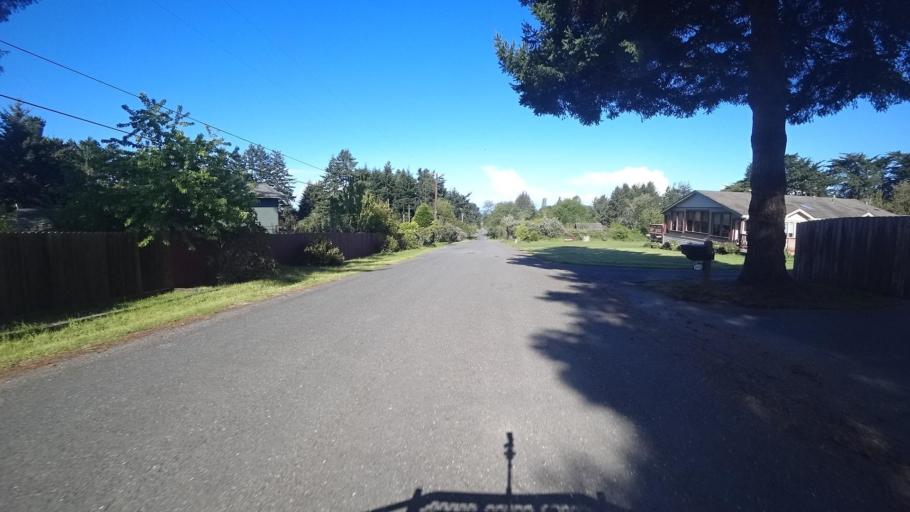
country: US
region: California
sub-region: Humboldt County
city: McKinleyville
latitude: 40.9634
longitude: -124.0930
